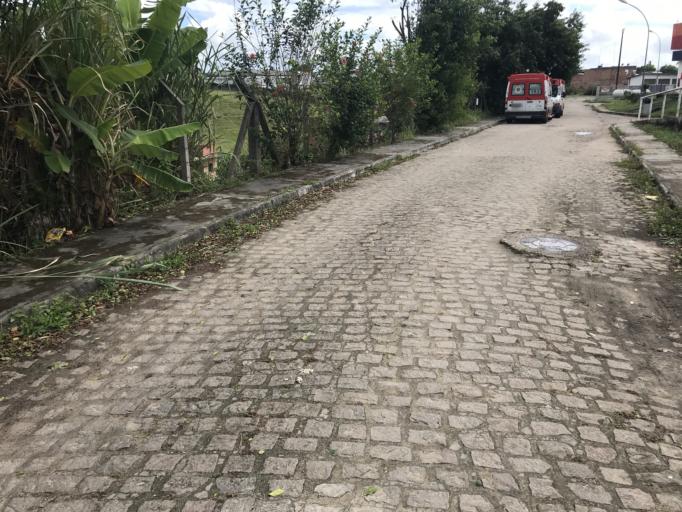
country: BR
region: Bahia
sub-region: Santo Antonio De Jesus
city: Santo Antonio de Jesus
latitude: -12.9810
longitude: -39.2819
